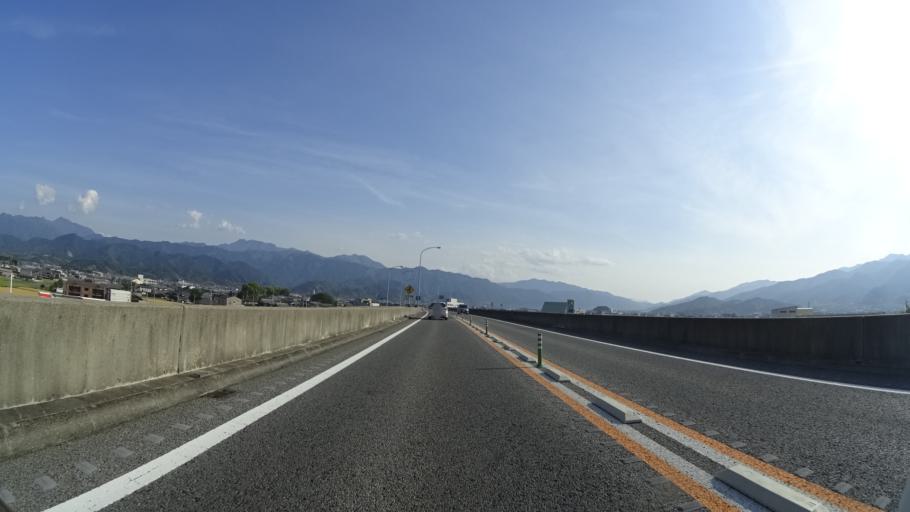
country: JP
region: Ehime
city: Saijo
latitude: 33.9174
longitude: 133.0735
